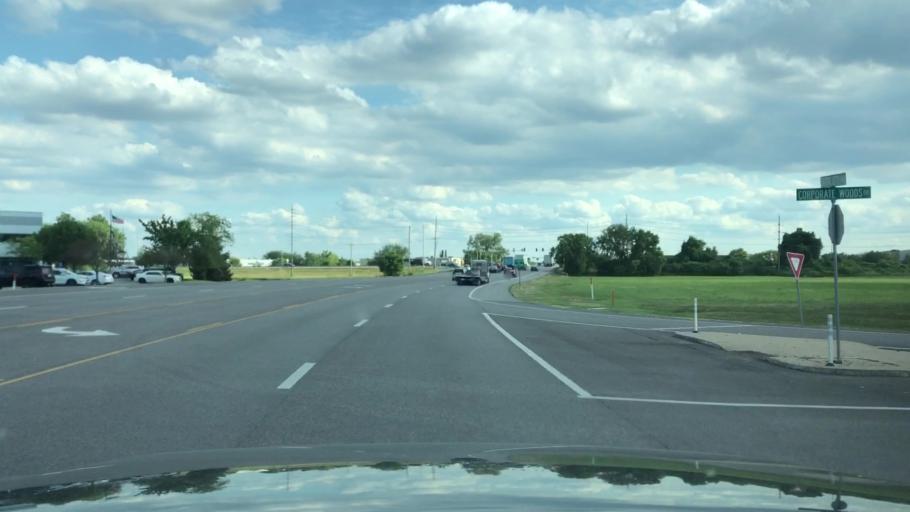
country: US
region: Missouri
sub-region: Saint Charles County
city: Saint Charles
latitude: 38.7818
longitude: -90.4590
